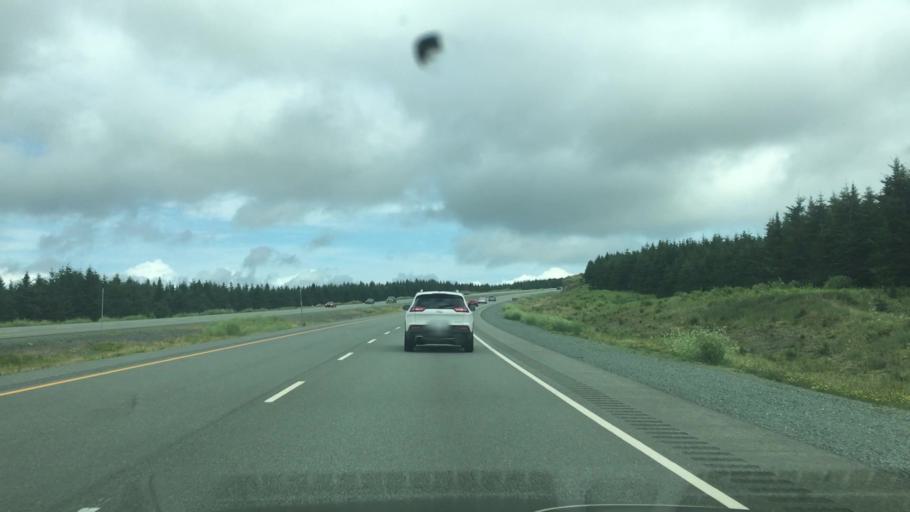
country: CA
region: Nova Scotia
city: Oxford
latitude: 45.5526
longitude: -63.7141
